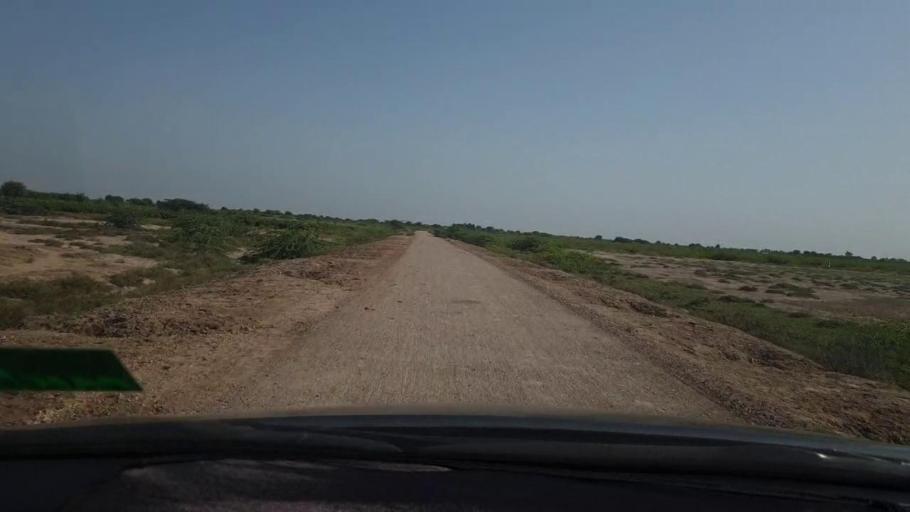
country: PK
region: Sindh
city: Naukot
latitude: 24.9406
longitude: 69.2447
